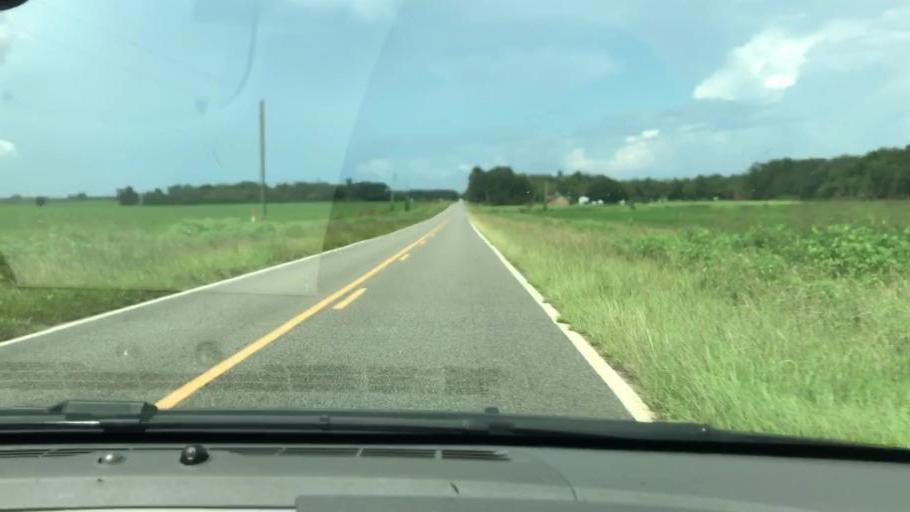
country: US
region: Georgia
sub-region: Seminole County
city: Donalsonville
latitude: 31.1028
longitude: -84.9961
